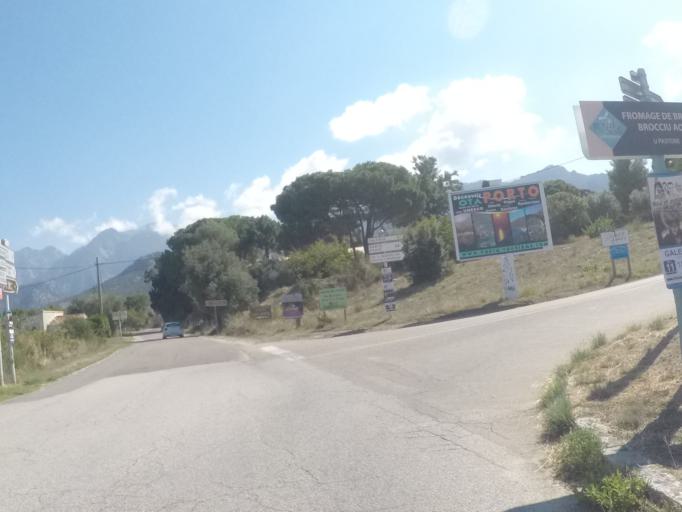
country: FR
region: Corsica
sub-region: Departement de la Haute-Corse
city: Calenzana
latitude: 42.4901
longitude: 8.7973
